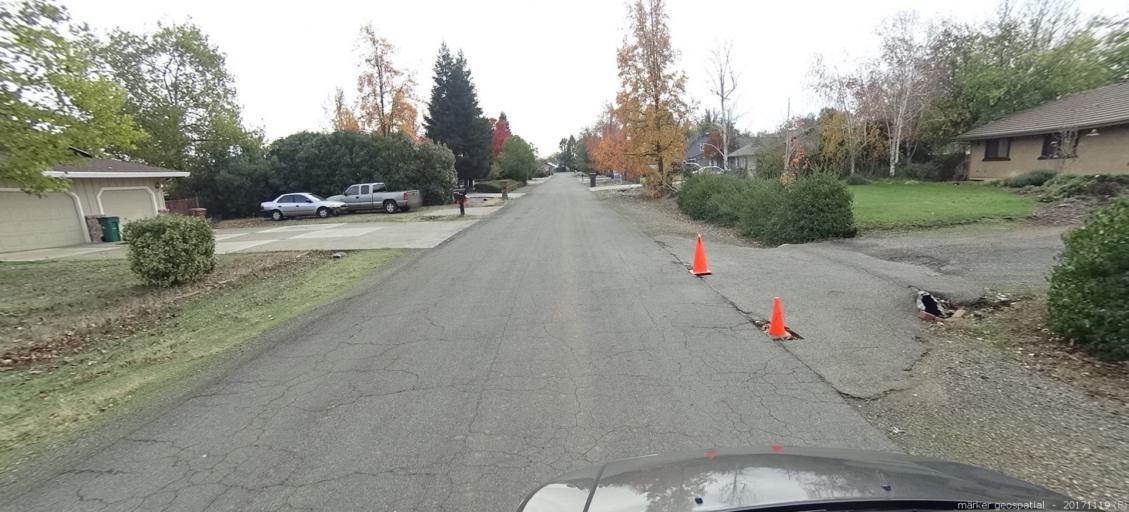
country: US
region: California
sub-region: Shasta County
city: Anderson
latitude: 40.4795
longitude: -122.2706
